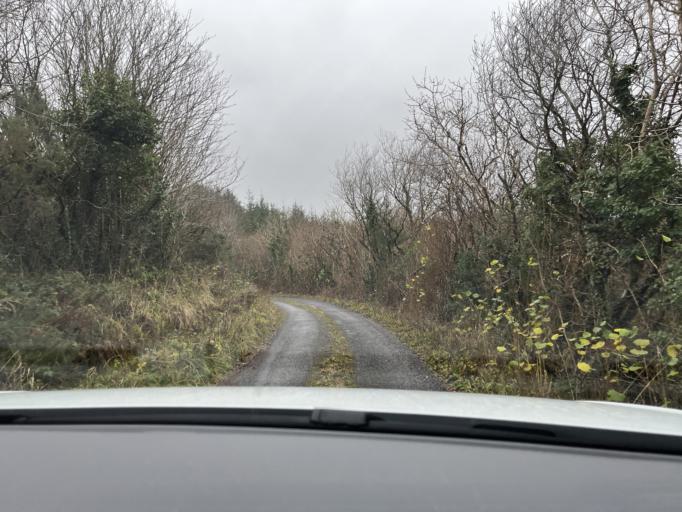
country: IE
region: Connaught
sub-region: County Leitrim
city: Manorhamilton
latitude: 54.2833
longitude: -8.1072
